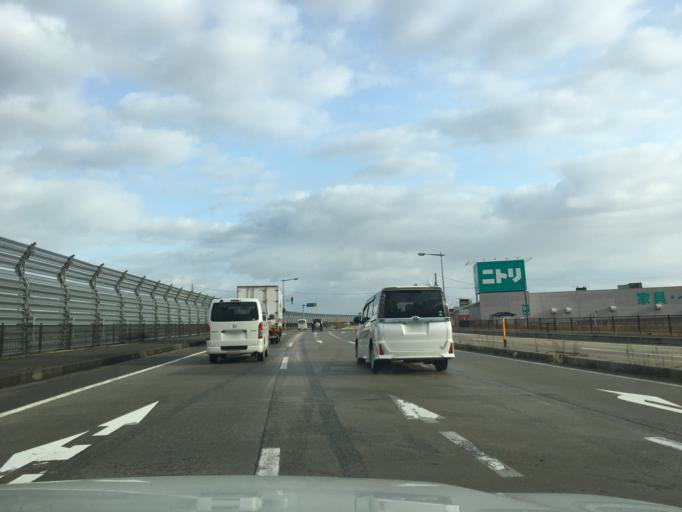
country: JP
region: Yamagata
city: Tsuruoka
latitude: 38.8176
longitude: 139.8330
